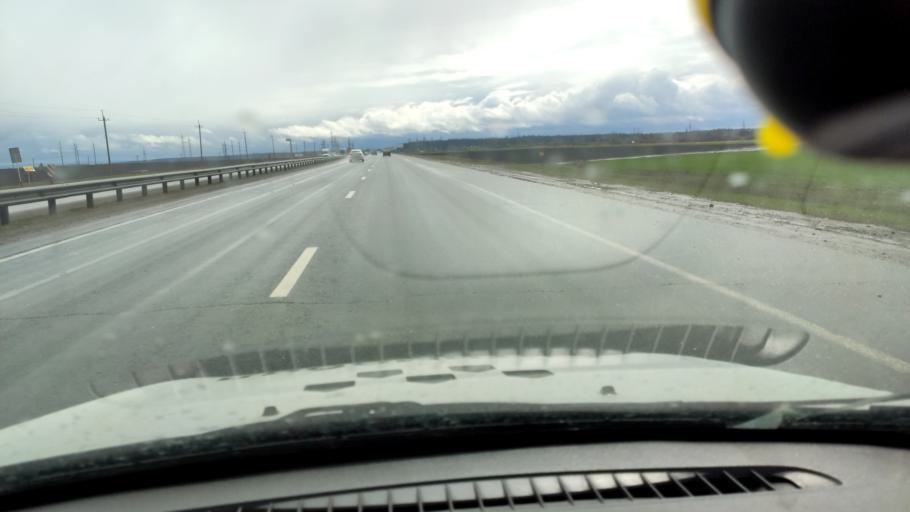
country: RU
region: Samara
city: Zhigulevsk
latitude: 53.5528
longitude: 49.5065
